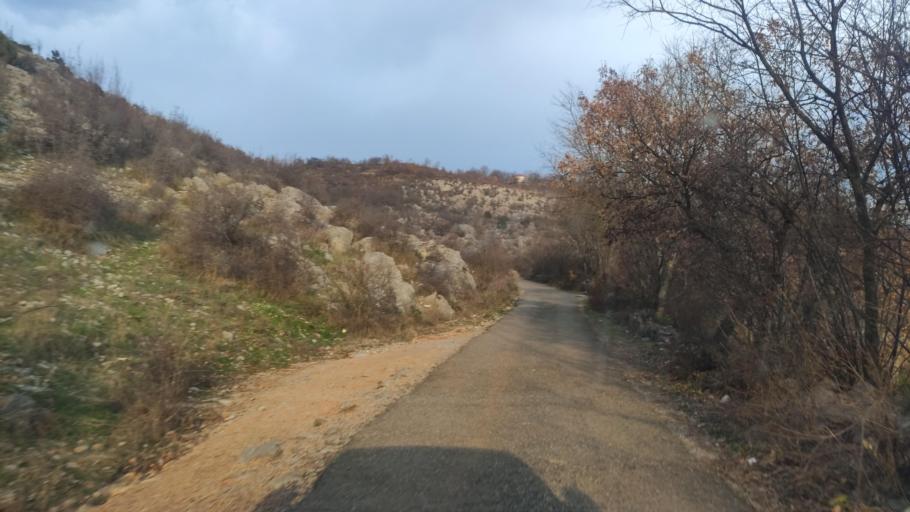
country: AL
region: Shkoder
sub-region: Rrethi i Malesia e Madhe
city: Gruemire
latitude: 42.2386
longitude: 19.5331
